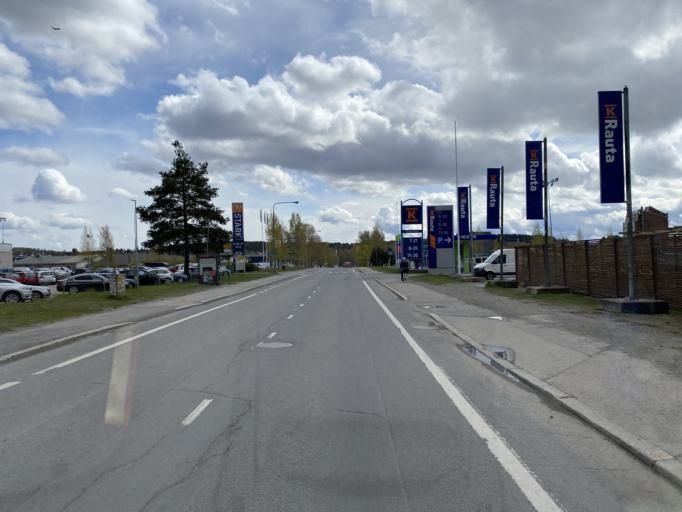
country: FI
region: Pirkanmaa
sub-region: Tampere
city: Tampere
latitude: 61.4804
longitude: 23.7826
